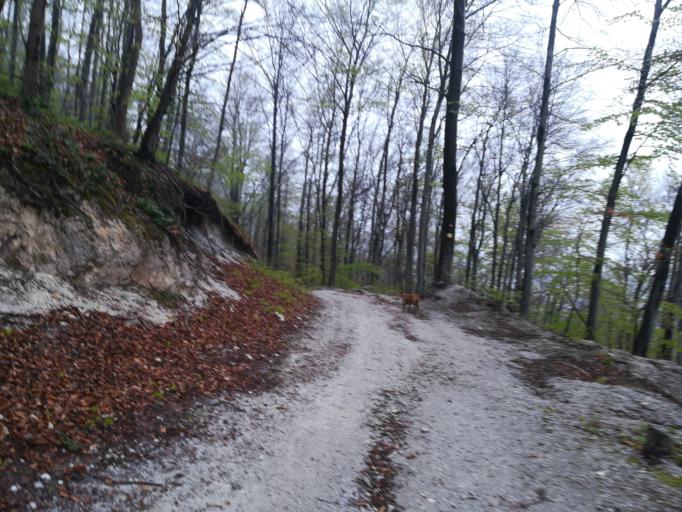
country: HR
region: Varazdinska
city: Ivanec
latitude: 46.1888
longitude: 16.1488
